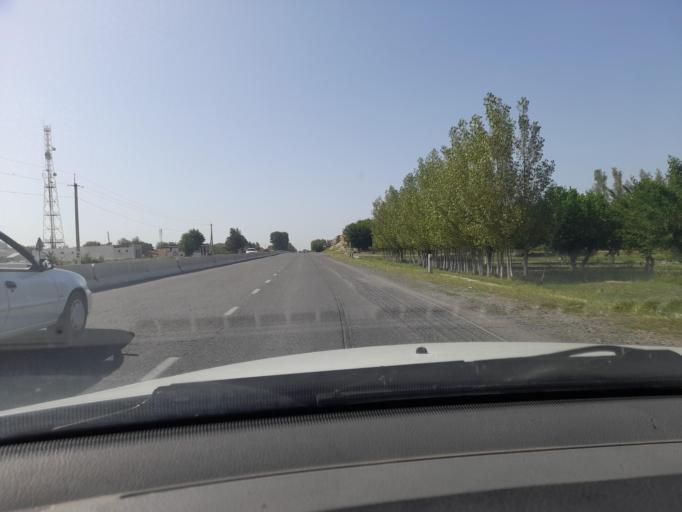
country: UZ
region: Samarqand
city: Daxbet
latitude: 39.8120
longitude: 66.8540
